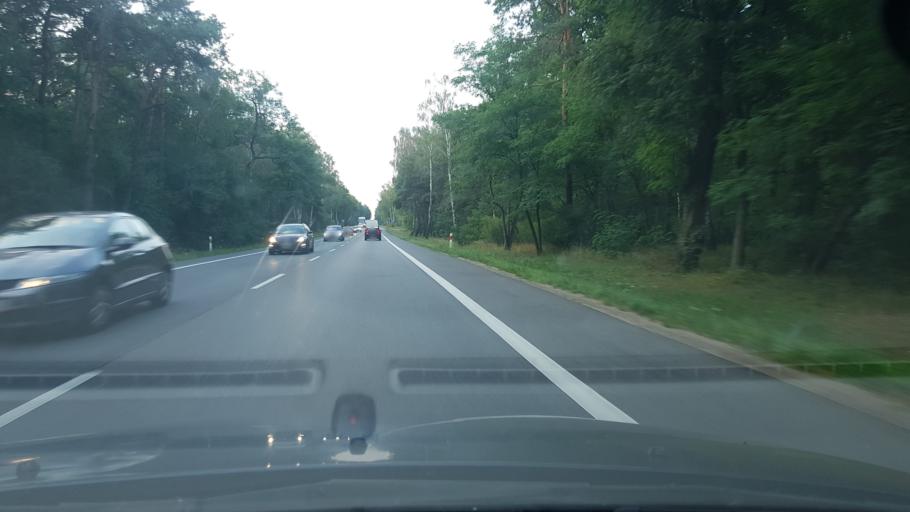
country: PL
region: Masovian Voivodeship
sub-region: Powiat mlawski
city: Strzegowo
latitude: 52.9069
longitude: 20.2868
